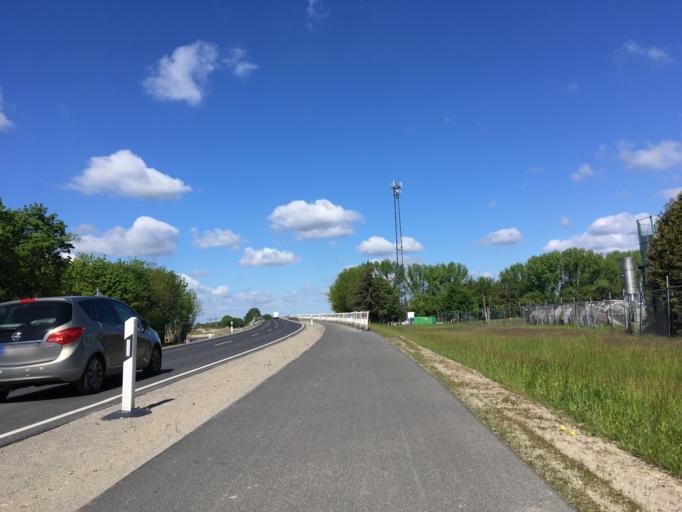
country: DE
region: Berlin
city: Blankenfelde
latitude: 52.6614
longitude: 13.4131
